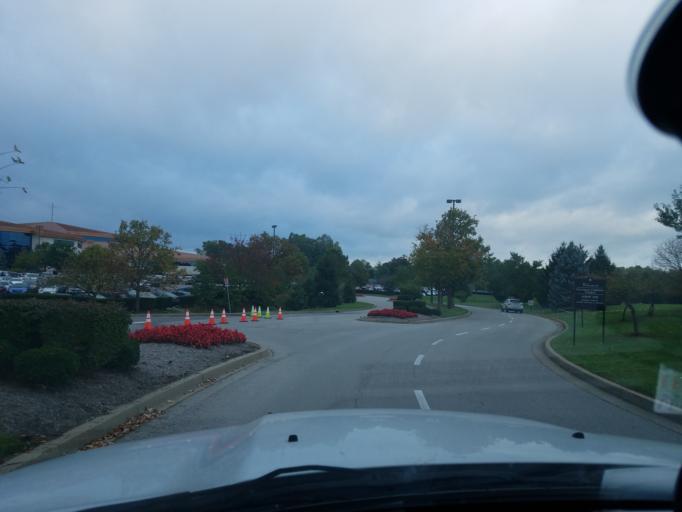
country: US
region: Kentucky
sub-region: Jefferson County
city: Douglass Hills
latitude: 38.2292
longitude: -85.5424
